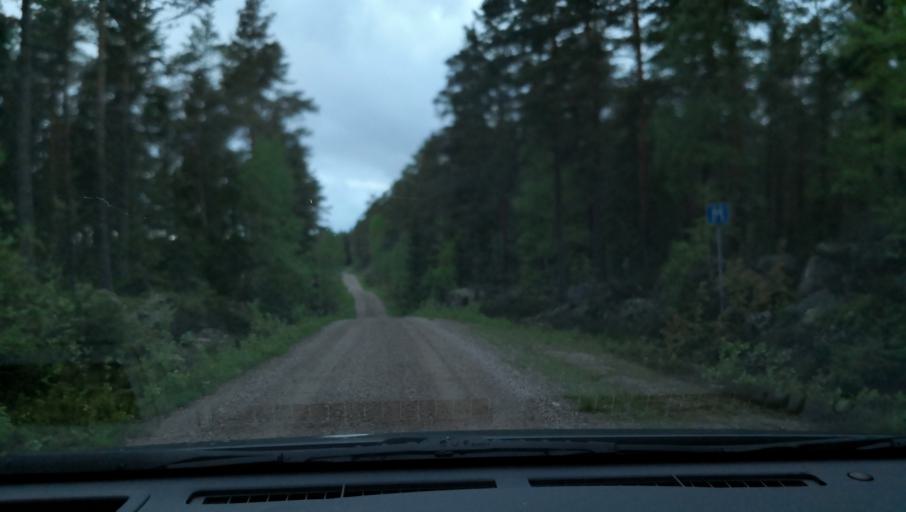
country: SE
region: Uppsala
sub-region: Heby Kommun
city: OEstervala
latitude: 59.9716
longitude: 17.2580
